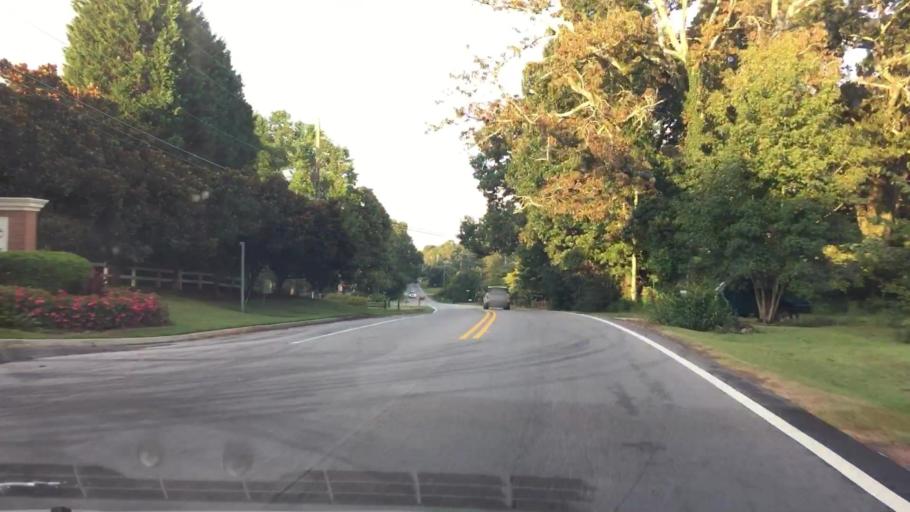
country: US
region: Georgia
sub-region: Henry County
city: McDonough
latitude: 33.4836
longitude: -84.1844
